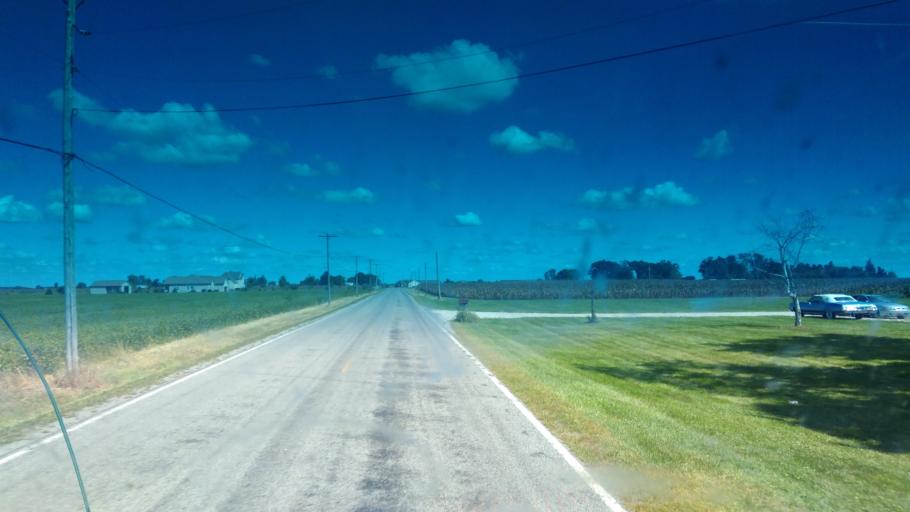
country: US
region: Ohio
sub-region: Madison County
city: Choctaw Lake
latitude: 40.0294
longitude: -83.3744
